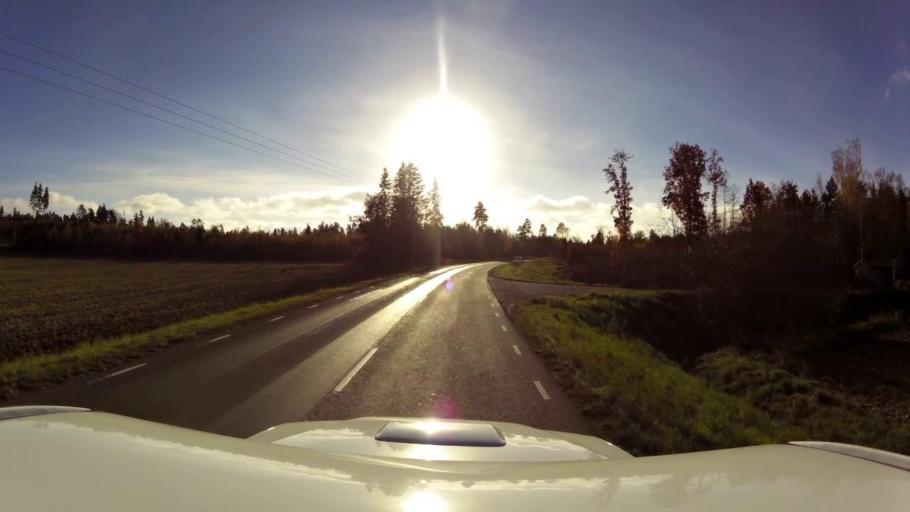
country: SE
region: OEstergoetland
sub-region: Linkopings Kommun
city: Vikingstad
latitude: 58.2958
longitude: 15.4669
